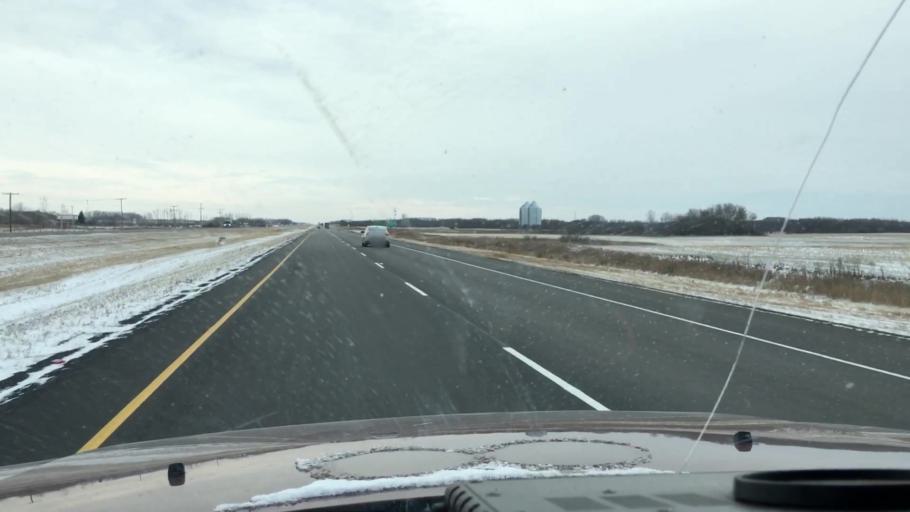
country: CA
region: Saskatchewan
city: Saskatoon
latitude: 52.0020
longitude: -106.5690
